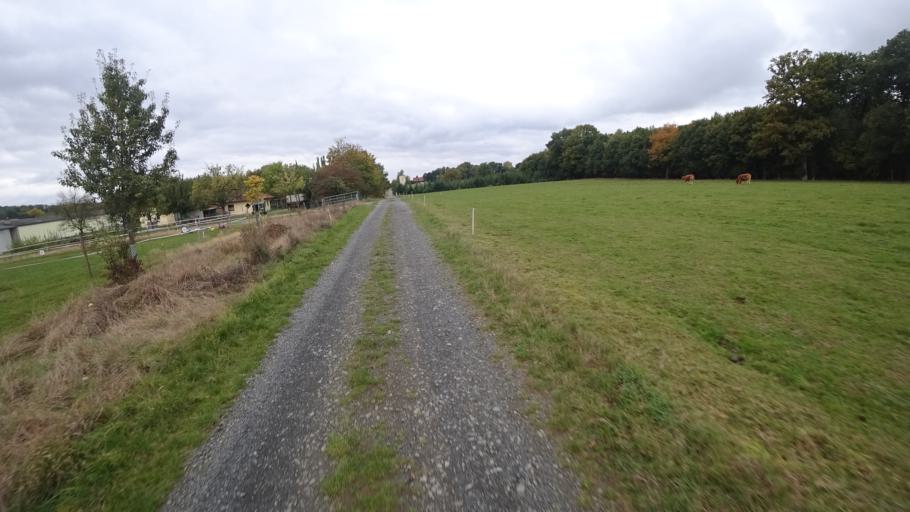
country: DE
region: Rheinland-Pfalz
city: Marienrachdorf
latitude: 50.5559
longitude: 7.7218
